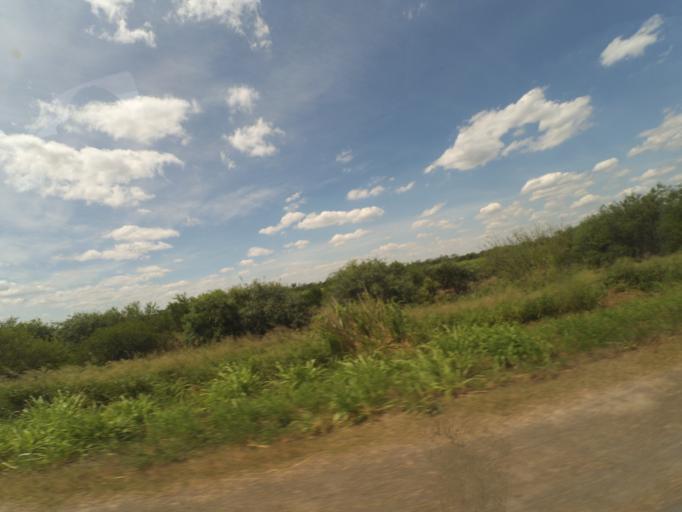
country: BO
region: Santa Cruz
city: Pailon
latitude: -17.5895
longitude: -61.9478
